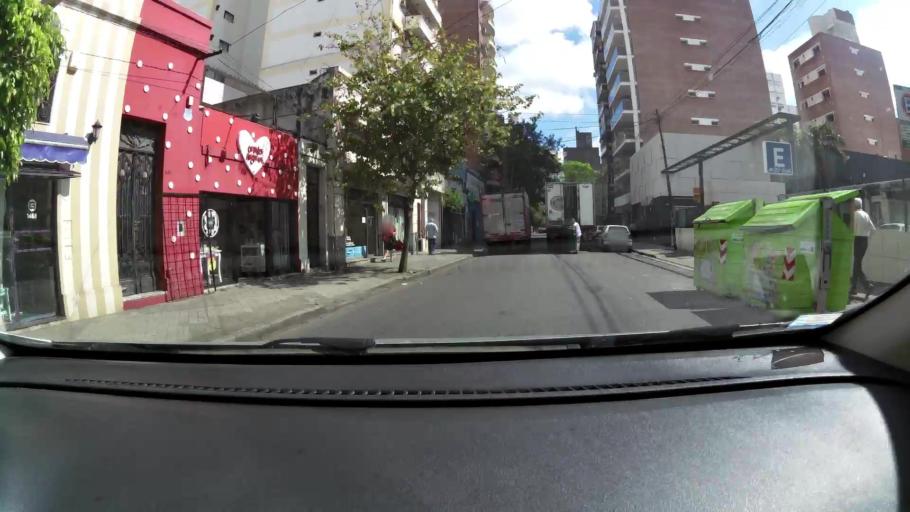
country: AR
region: Santa Fe
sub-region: Departamento de Rosario
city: Rosario
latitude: -32.9537
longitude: -60.6473
